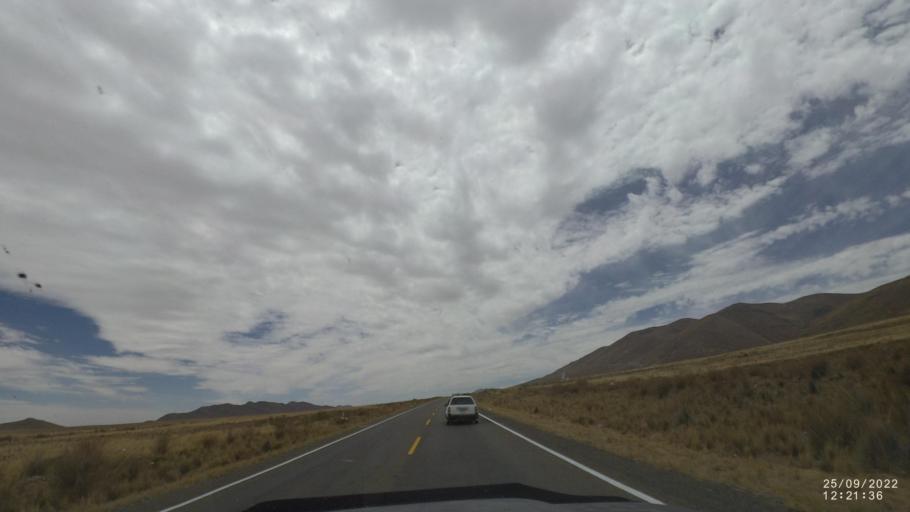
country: BO
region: Oruro
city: Poopo
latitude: -18.4085
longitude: -66.9766
